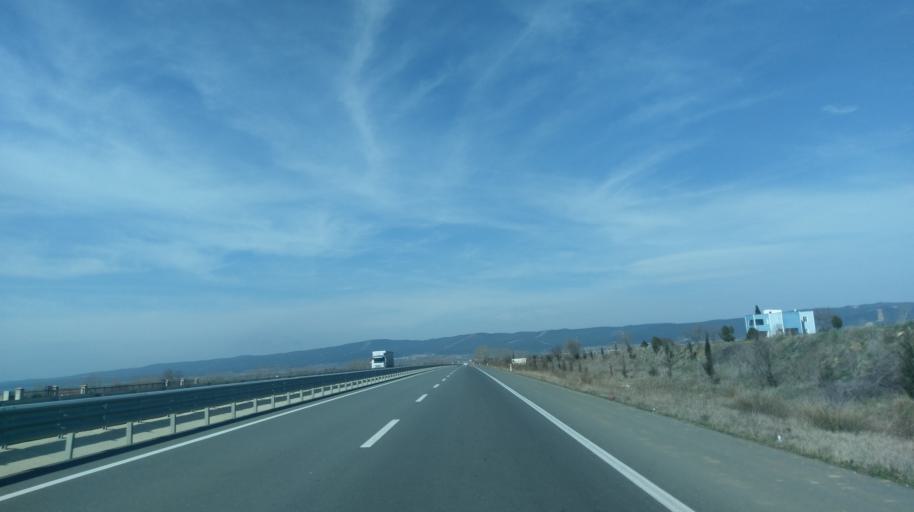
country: TR
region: Canakkale
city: Evrese
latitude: 40.6499
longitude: 26.8372
